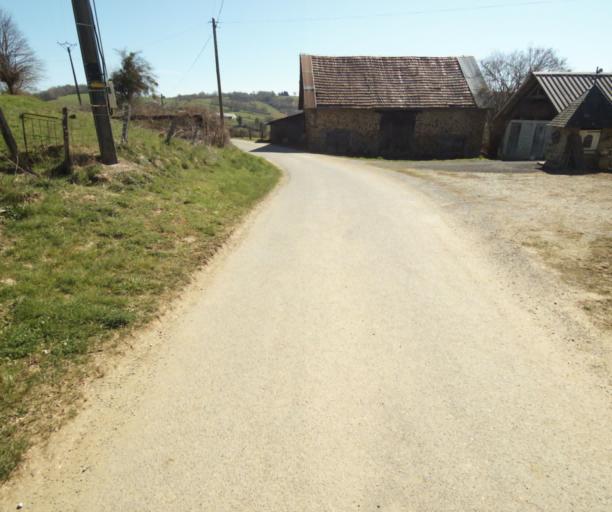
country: FR
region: Limousin
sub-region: Departement de la Correze
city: Chamboulive
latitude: 45.4513
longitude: 1.6654
